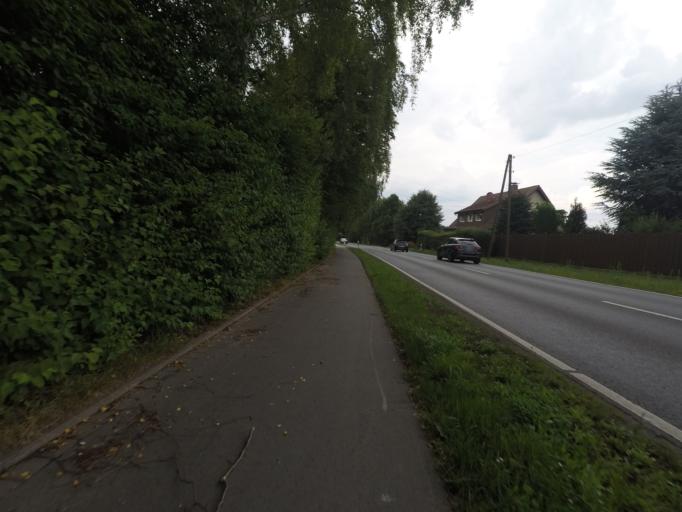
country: DE
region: North Rhine-Westphalia
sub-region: Regierungsbezirk Detmold
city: Hiddenhausen
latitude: 52.1384
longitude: 8.6235
